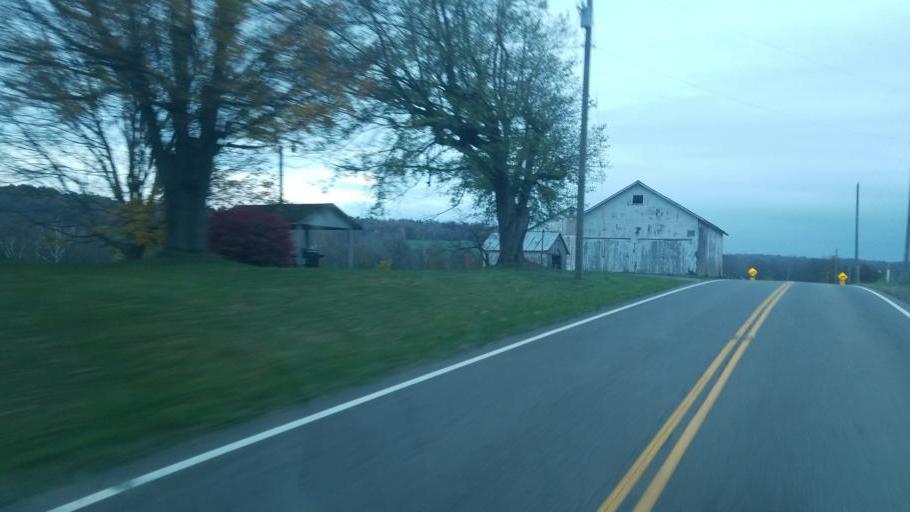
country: US
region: Ohio
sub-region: Sandusky County
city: Bellville
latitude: 40.6015
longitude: -82.4130
